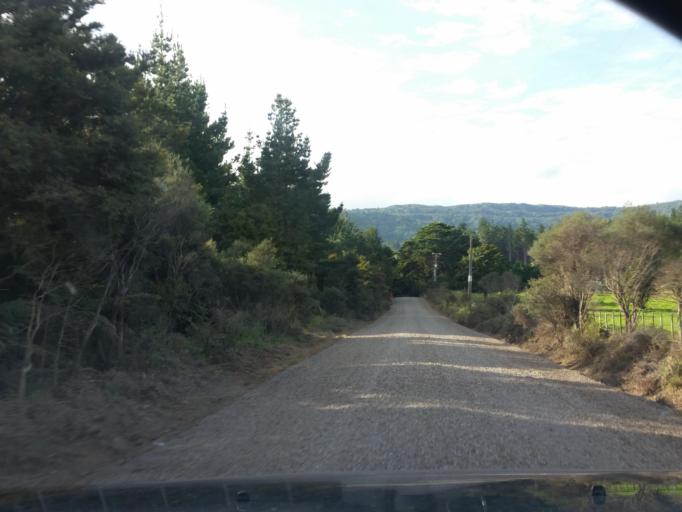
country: NZ
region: Northland
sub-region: Kaipara District
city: Dargaville
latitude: -35.7717
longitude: 173.7168
